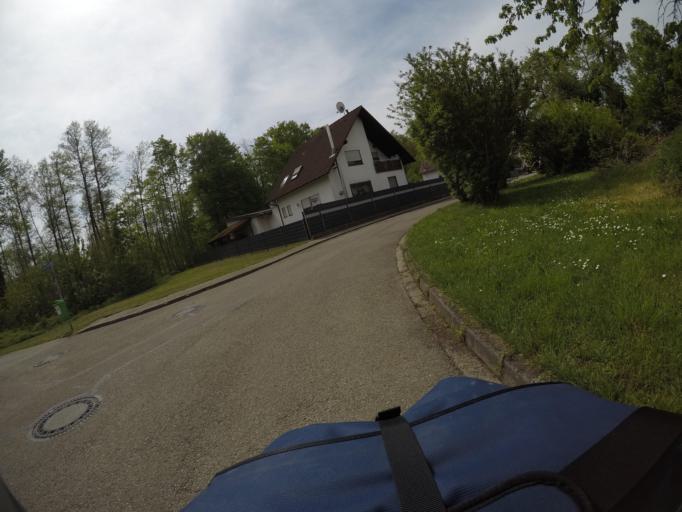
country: DE
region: Baden-Wuerttemberg
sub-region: Karlsruhe Region
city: Lichtenau
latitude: 48.7372
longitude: 7.9867
